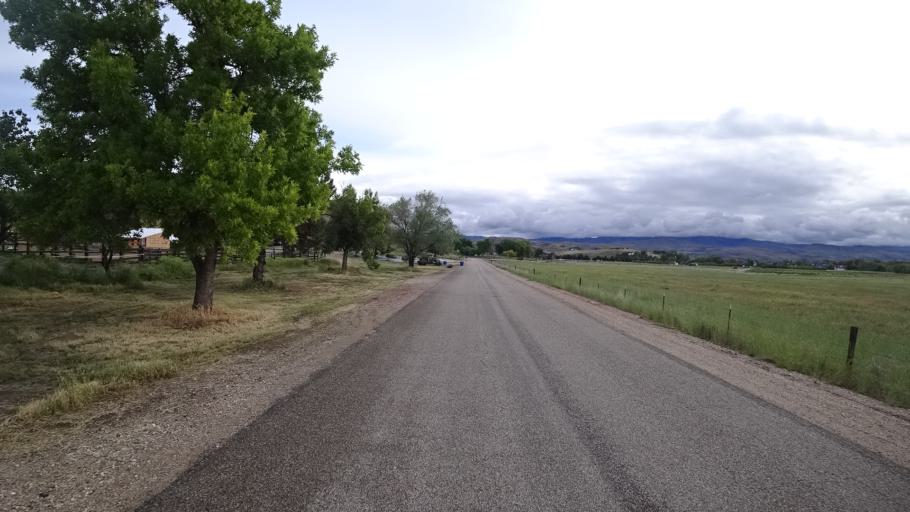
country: US
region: Idaho
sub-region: Ada County
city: Eagle
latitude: 43.7343
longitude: -116.3111
